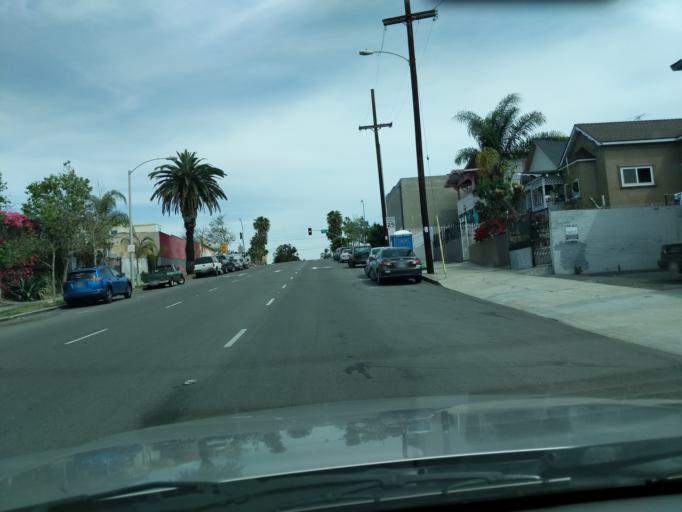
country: US
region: California
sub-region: San Diego County
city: San Diego
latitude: 32.7054
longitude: -117.1467
